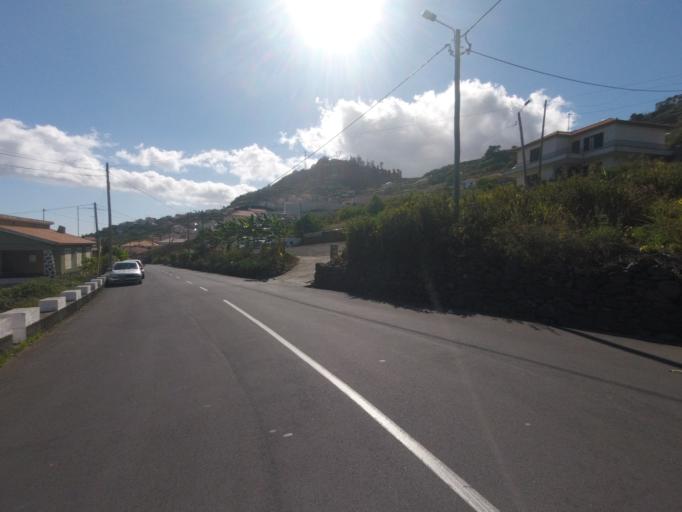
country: PT
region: Madeira
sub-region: Ribeira Brava
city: Campanario
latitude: 32.6748
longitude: -17.0268
